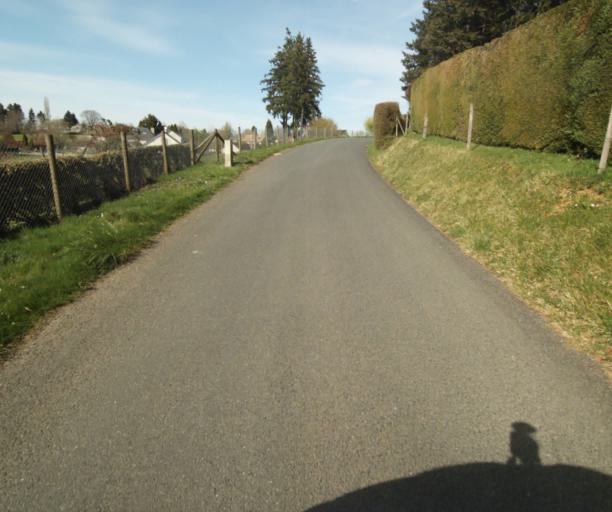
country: FR
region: Limousin
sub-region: Departement de la Correze
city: Naves
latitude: 45.3332
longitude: 1.7496
